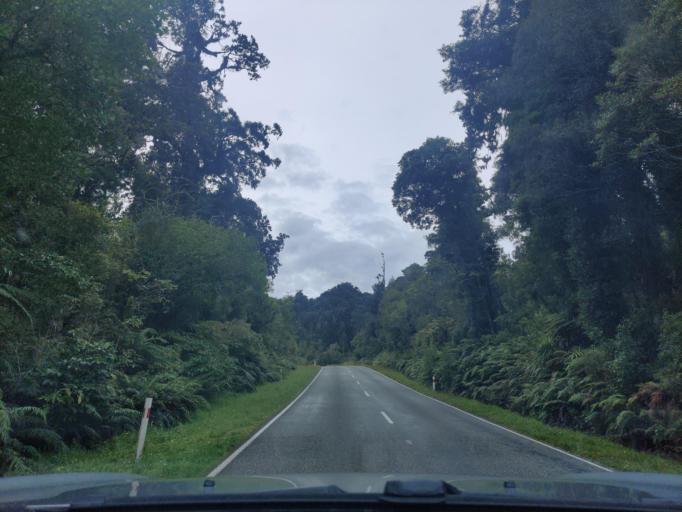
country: NZ
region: West Coast
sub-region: Westland District
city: Hokitika
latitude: -42.9470
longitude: 170.7540
